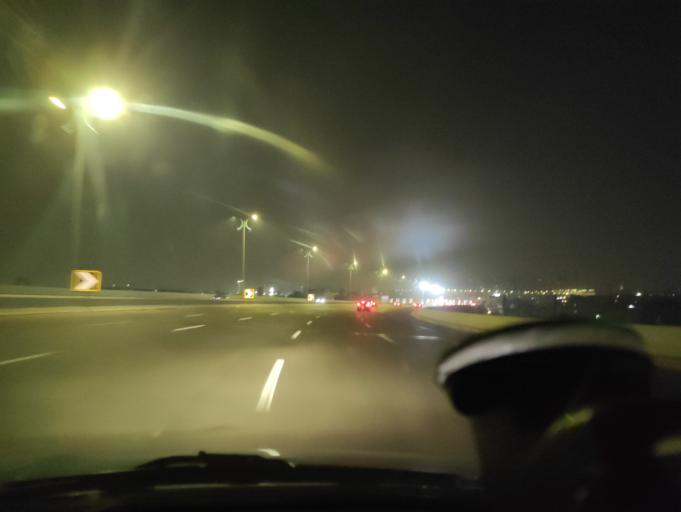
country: EG
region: Muhafazat al Qahirah
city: Cairo
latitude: 30.1124
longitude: 31.2211
